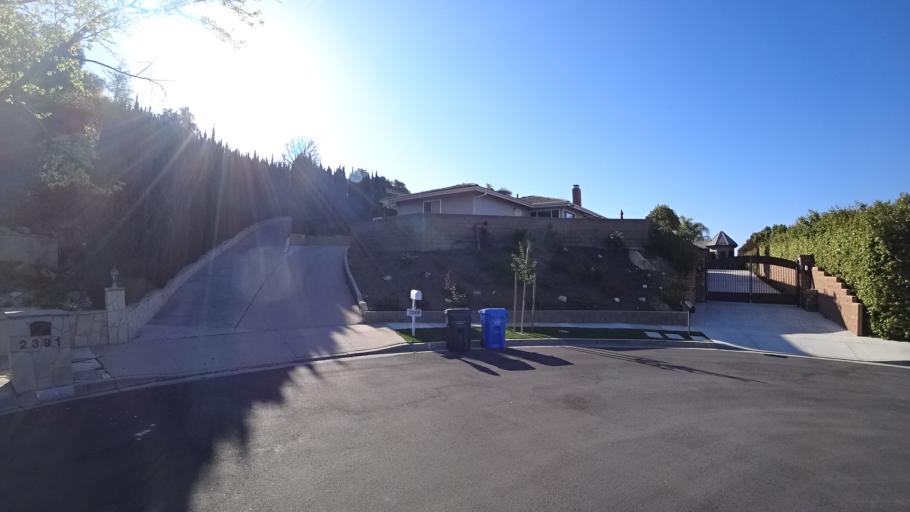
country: US
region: California
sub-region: Ventura County
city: Thousand Oaks
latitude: 34.1924
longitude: -118.8365
